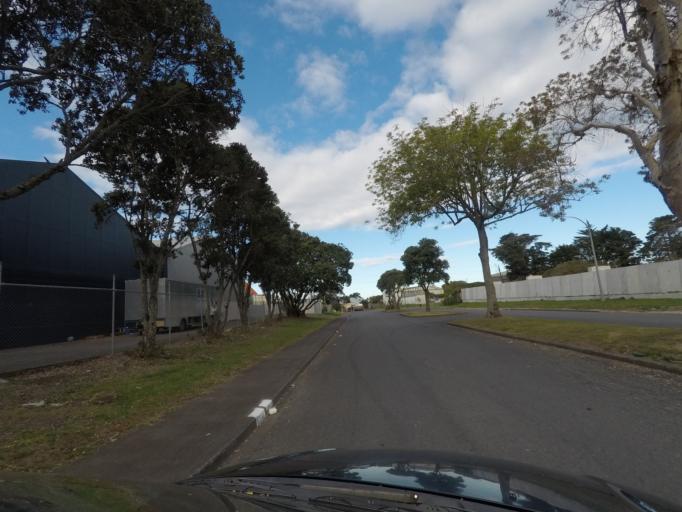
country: NZ
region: Auckland
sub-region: Auckland
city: Rosebank
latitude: -36.8890
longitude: 174.6613
